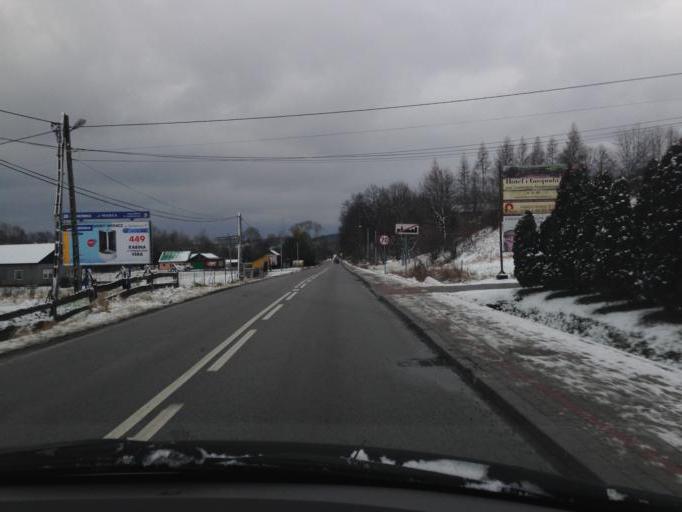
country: PL
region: Lesser Poland Voivodeship
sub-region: Powiat brzeski
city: Iwkowa
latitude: 49.8590
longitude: 20.5402
